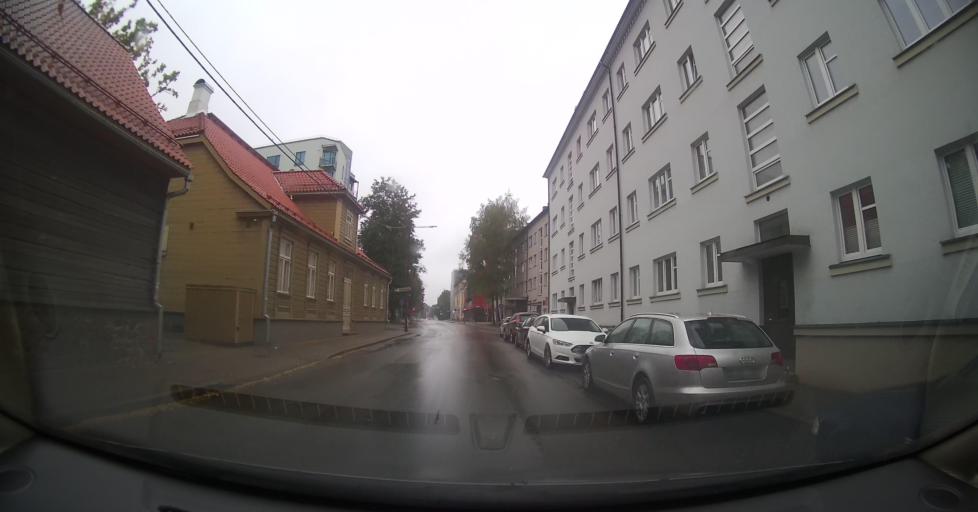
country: EE
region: Tartu
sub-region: Tartu linn
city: Tartu
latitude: 58.3746
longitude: 26.7292
